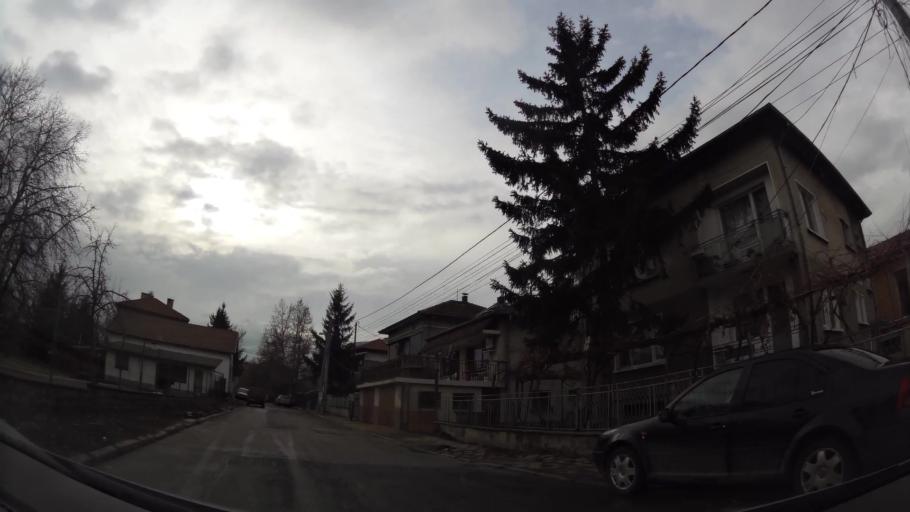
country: BG
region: Sofiya
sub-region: Obshtina Bozhurishte
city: Bozhurishte
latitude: 42.7440
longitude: 23.2640
